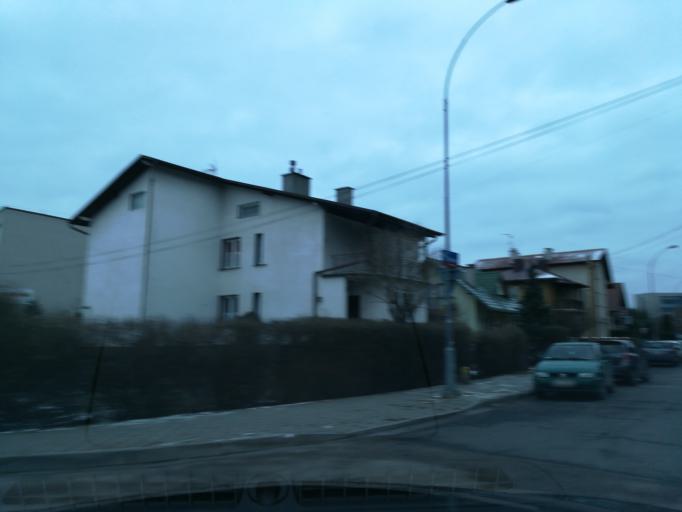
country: PL
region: Subcarpathian Voivodeship
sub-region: Rzeszow
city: Rzeszow
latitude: 50.0327
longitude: 22.0241
